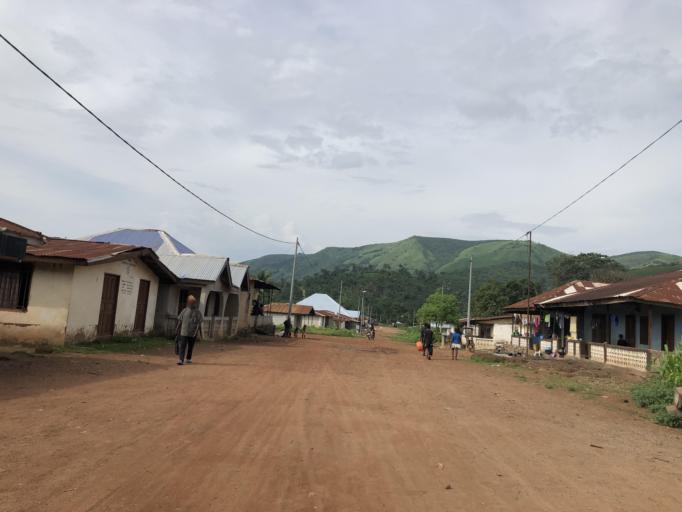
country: SL
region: Northern Province
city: Bumbuna
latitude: 9.0442
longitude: -11.7452
